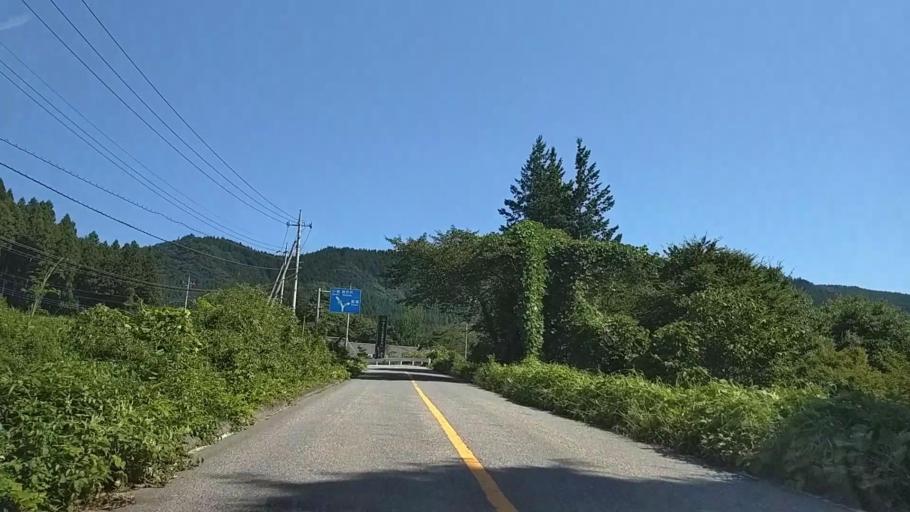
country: JP
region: Gunma
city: Annaka
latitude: 36.3537
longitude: 138.7161
